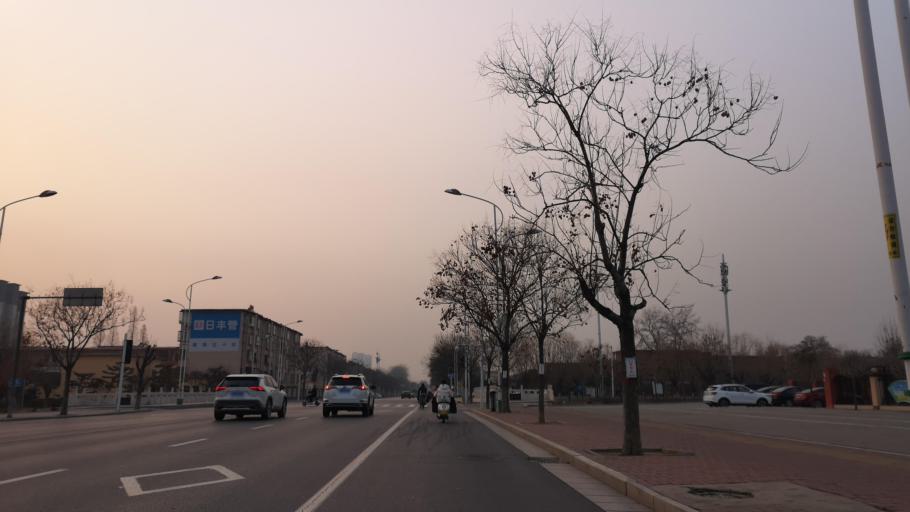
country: CN
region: Henan Sheng
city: Zhongyuanlu
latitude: 35.7842
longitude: 115.0776
